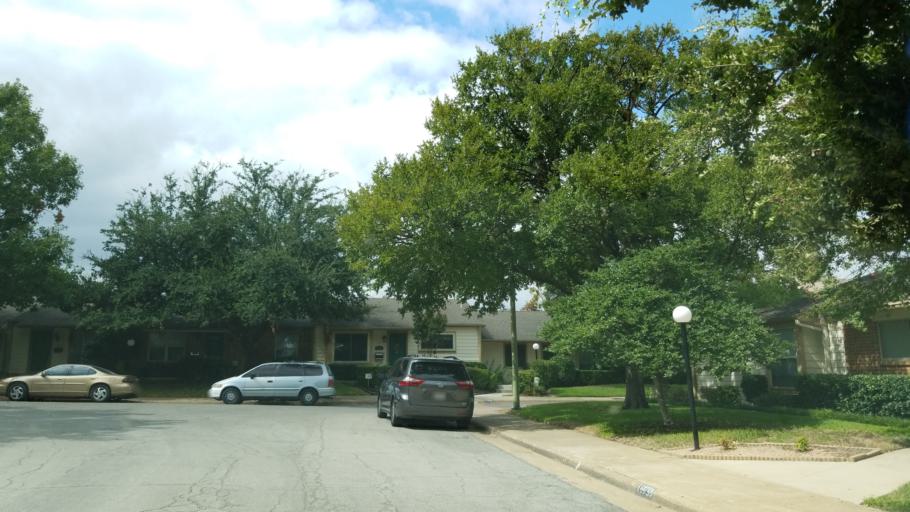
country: US
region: Texas
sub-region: Dallas County
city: Richardson
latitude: 32.9344
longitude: -96.7671
